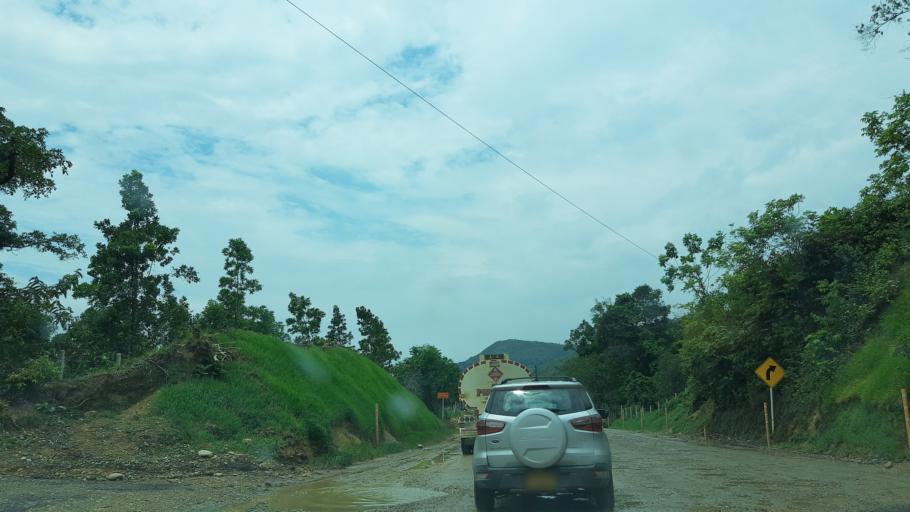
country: CO
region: Casanare
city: Sabanalarga
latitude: 4.7690
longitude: -73.0047
